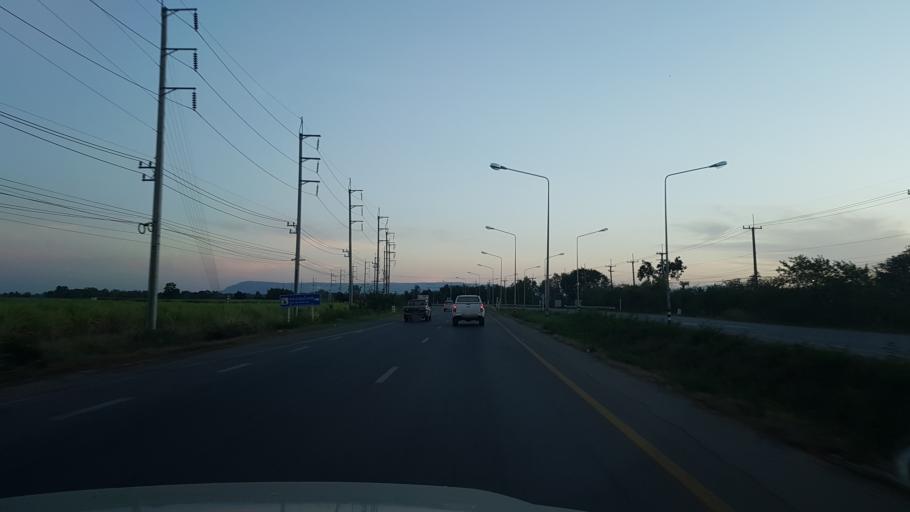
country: TH
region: Chaiyaphum
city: Phu Khiao
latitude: 16.4571
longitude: 102.1223
